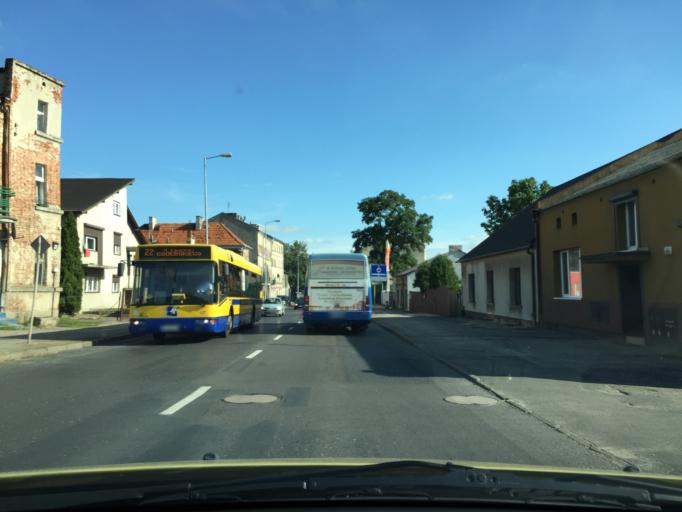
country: PL
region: Greater Poland Voivodeship
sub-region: Kalisz
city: Kalisz
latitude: 51.7723
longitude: 18.0924
